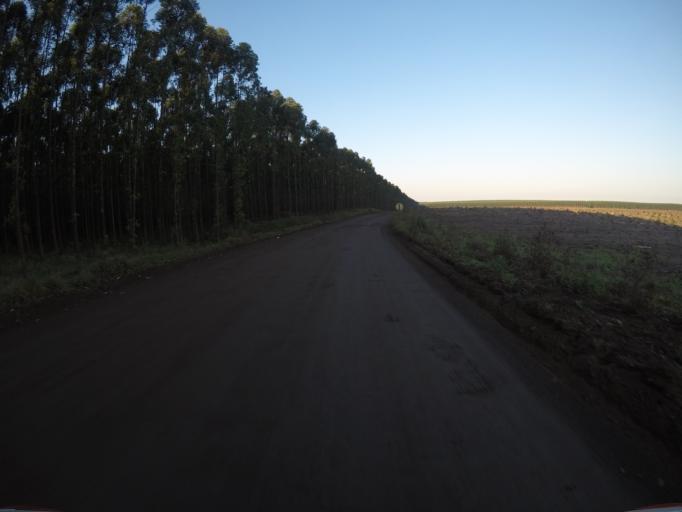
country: ZA
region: KwaZulu-Natal
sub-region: uThungulu District Municipality
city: KwaMbonambi
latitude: -28.6724
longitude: 32.0991
